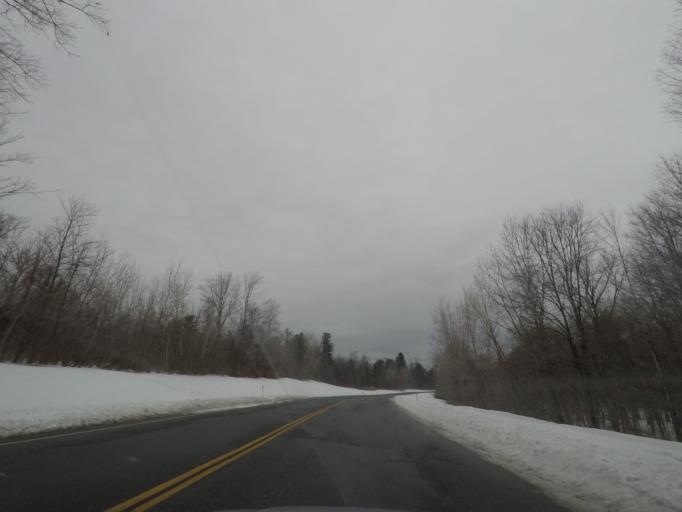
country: US
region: New York
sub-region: Schenectady County
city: Niskayuna
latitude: 42.7656
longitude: -73.8245
